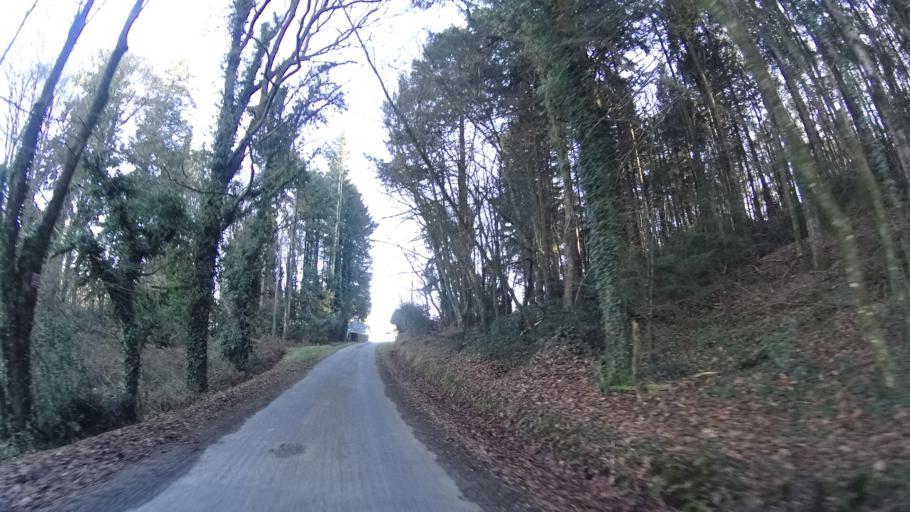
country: FR
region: Brittany
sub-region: Departement du Morbihan
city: Saint-Jacut-les-Pins
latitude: 47.6716
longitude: -2.2098
